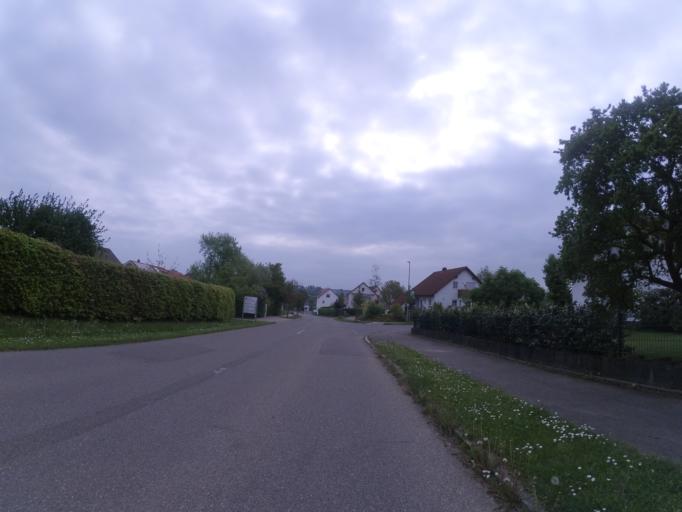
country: DE
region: Baden-Wuerttemberg
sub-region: Tuebingen Region
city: Staig
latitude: 48.3010
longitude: 9.9866
